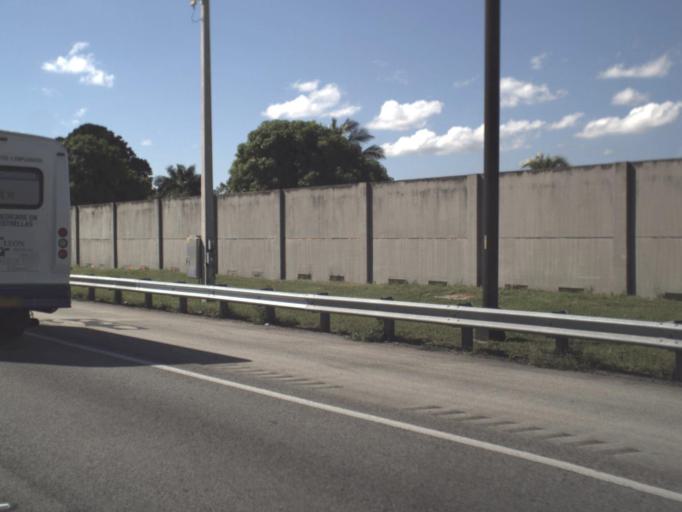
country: US
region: Florida
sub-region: Miami-Dade County
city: Westwood Lake
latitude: 25.7394
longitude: -80.3847
